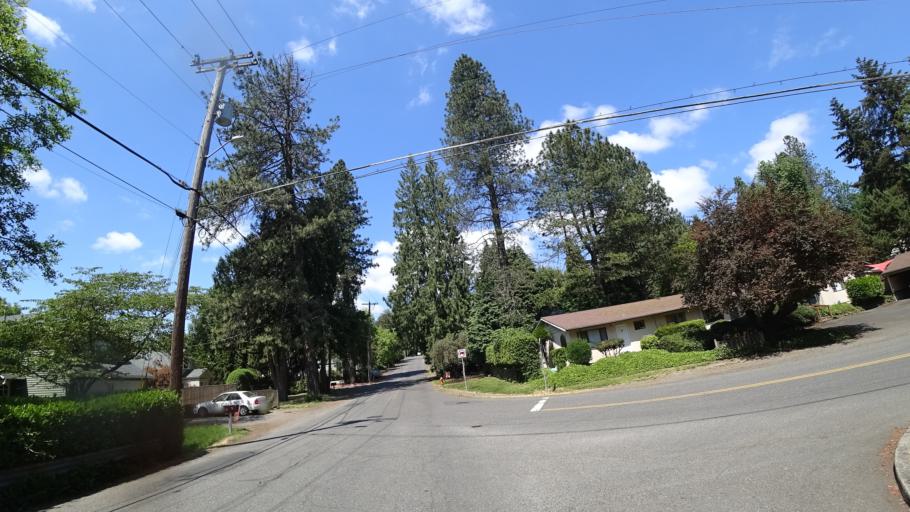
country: US
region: Oregon
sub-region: Washington County
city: Garden Home-Whitford
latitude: 45.4631
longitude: -122.7077
